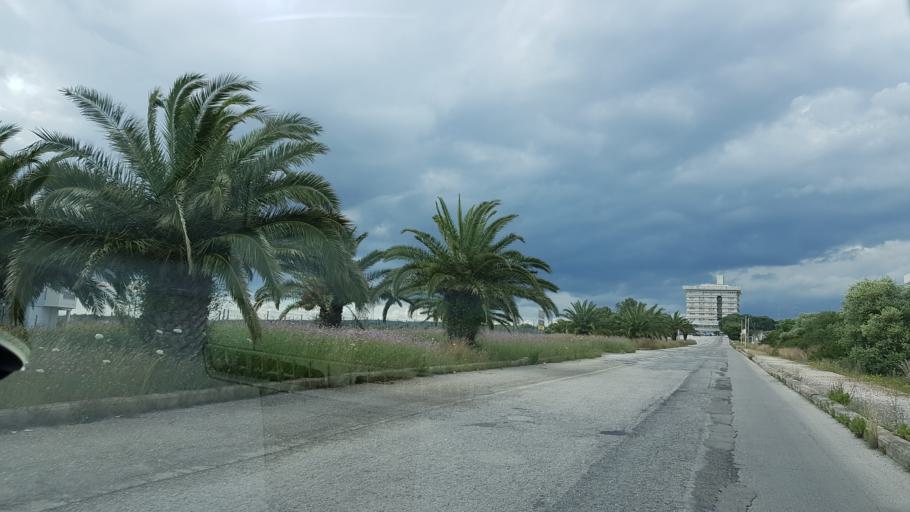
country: IT
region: Apulia
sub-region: Provincia di Taranto
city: Paolo VI
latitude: 40.5344
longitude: 17.2770
